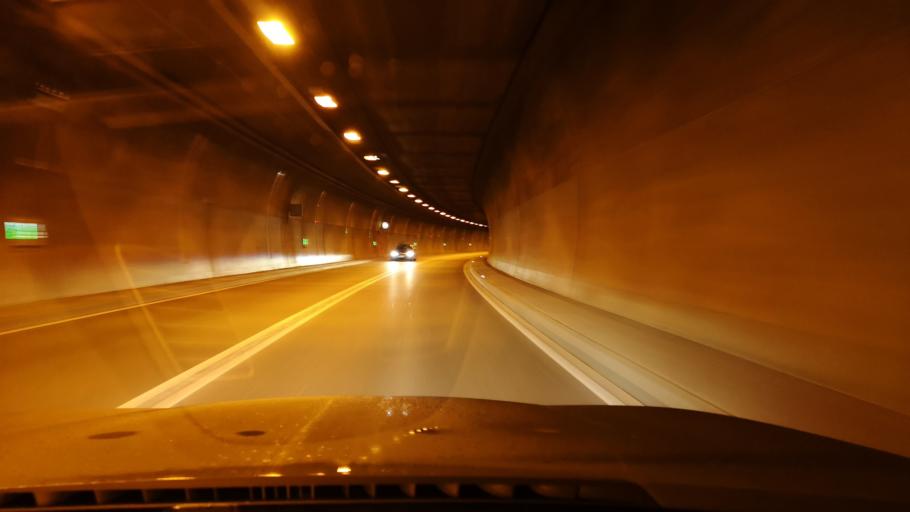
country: DE
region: Baden-Wuerttemberg
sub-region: Karlsruhe Region
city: Ettlingen
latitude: 48.9361
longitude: 8.4286
